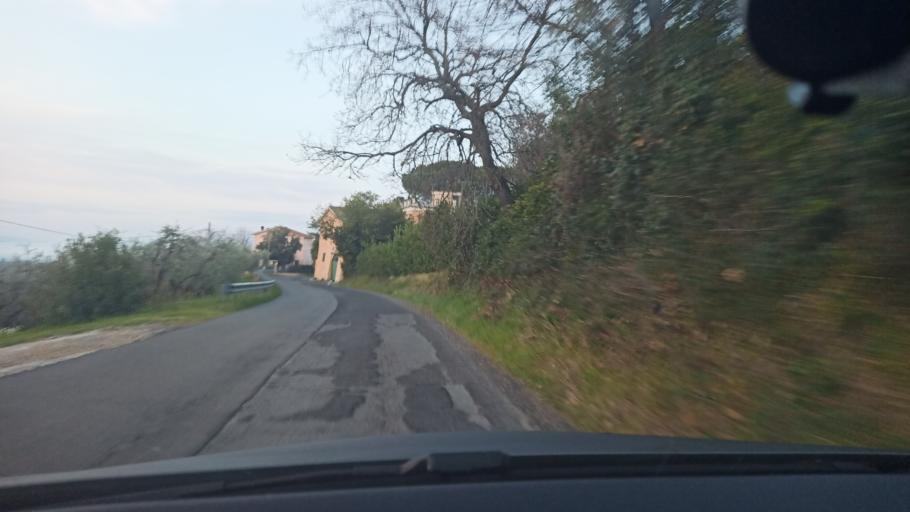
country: IT
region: Latium
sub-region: Provincia di Rieti
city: Torri in Sabina
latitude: 42.3393
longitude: 12.6503
